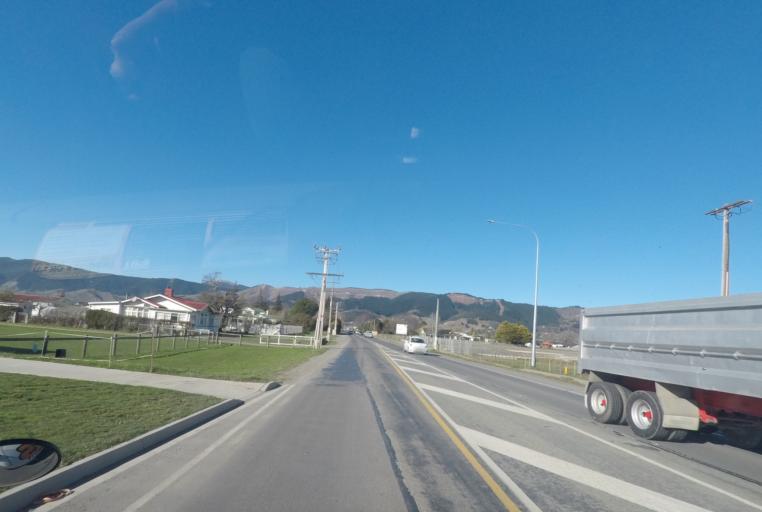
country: NZ
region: Tasman
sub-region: Tasman District
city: Richmond
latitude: -41.3300
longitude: 173.1746
